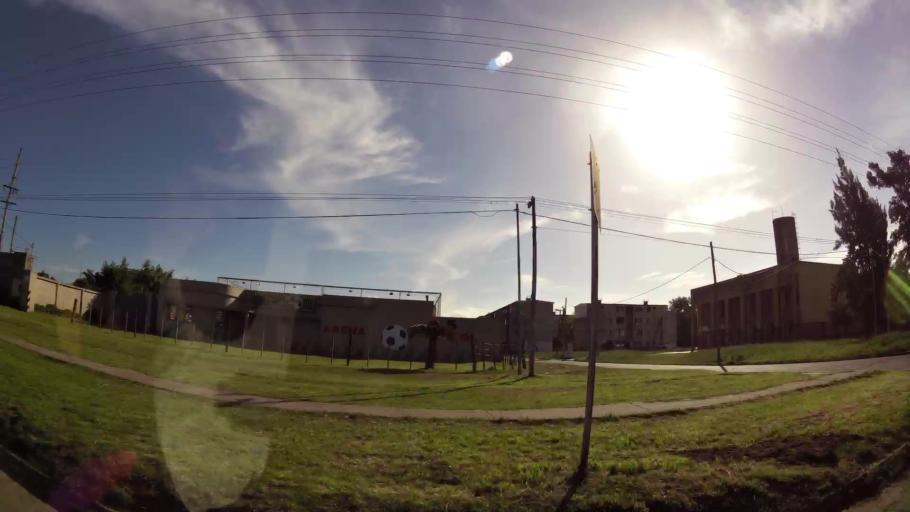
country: AR
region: Buenos Aires
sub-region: Partido de Quilmes
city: Quilmes
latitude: -34.7809
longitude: -58.2337
